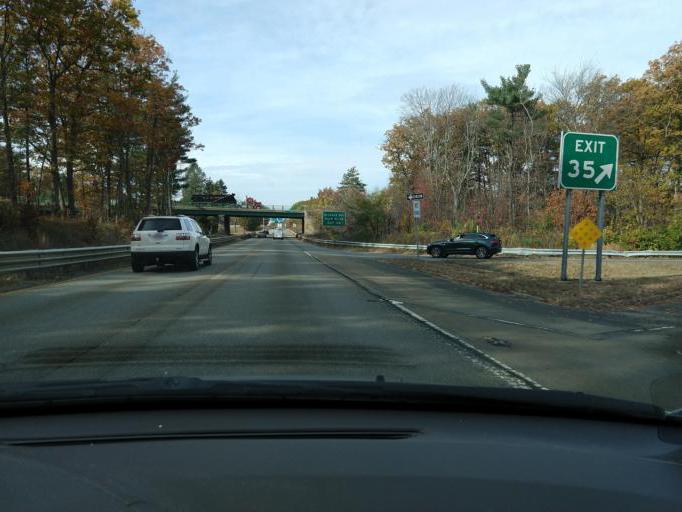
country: US
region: Massachusetts
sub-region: Middlesex County
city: Shirley
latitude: 42.5197
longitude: -71.6912
